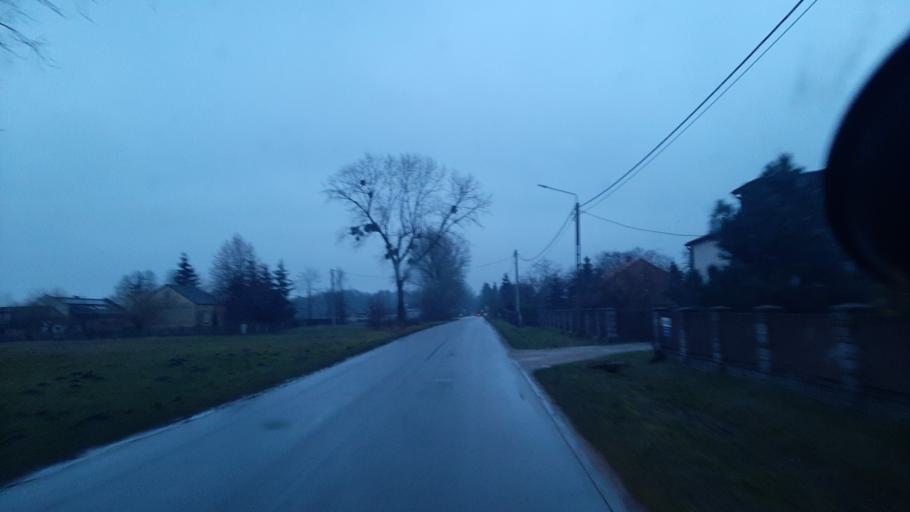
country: PL
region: Lublin Voivodeship
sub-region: Powiat lubelski
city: Garbow
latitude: 51.3920
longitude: 22.4108
